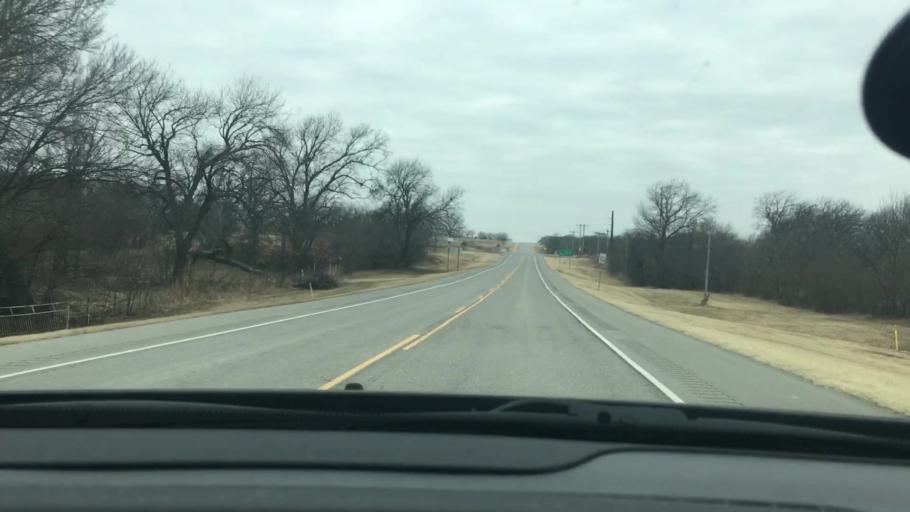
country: US
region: Oklahoma
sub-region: Carter County
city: Healdton
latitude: 34.4924
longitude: -97.4015
